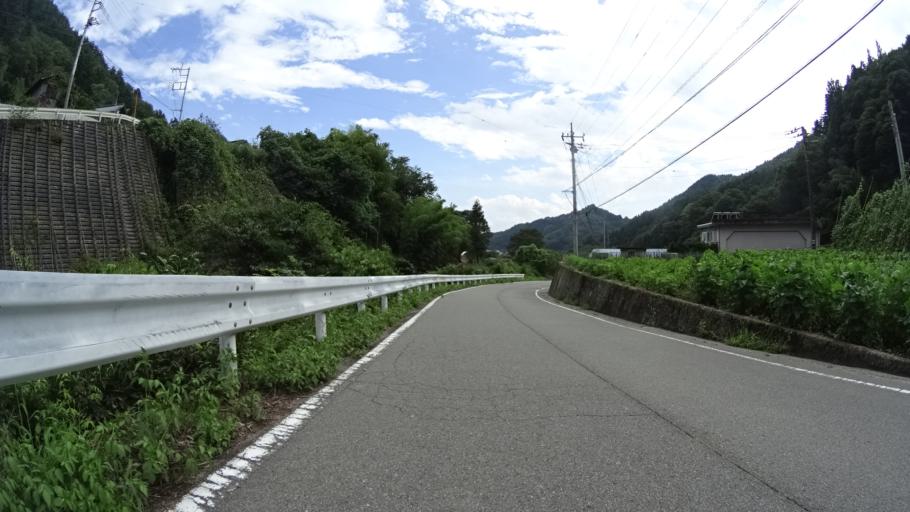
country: JP
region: Yamanashi
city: Nirasaki
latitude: 35.7718
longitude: 138.5331
